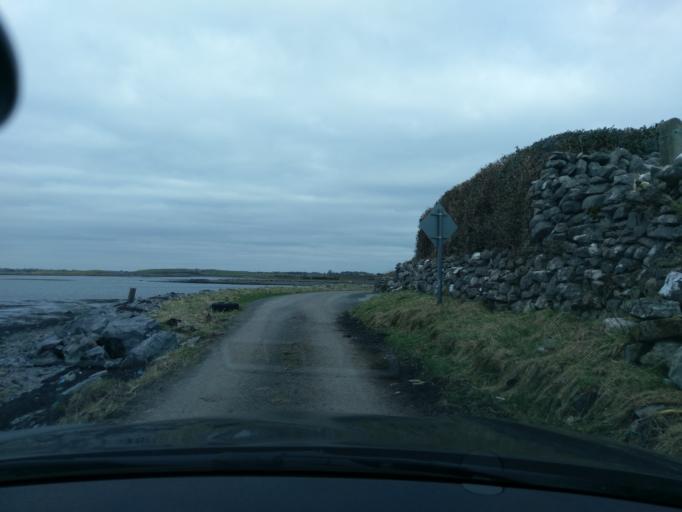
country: IE
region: Connaught
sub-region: County Galway
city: Oranmore
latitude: 53.1969
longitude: -8.9398
